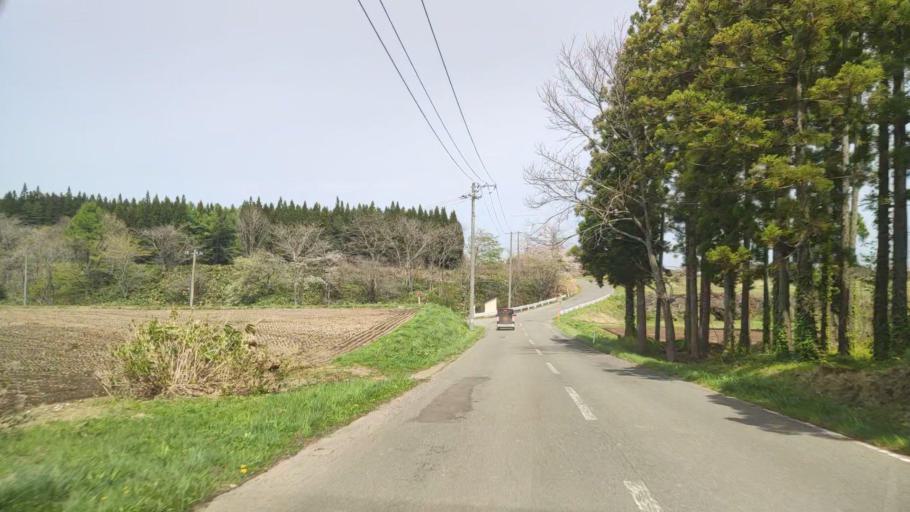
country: JP
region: Aomori
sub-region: Misawa Shi
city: Inuotose
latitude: 40.7666
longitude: 141.1198
